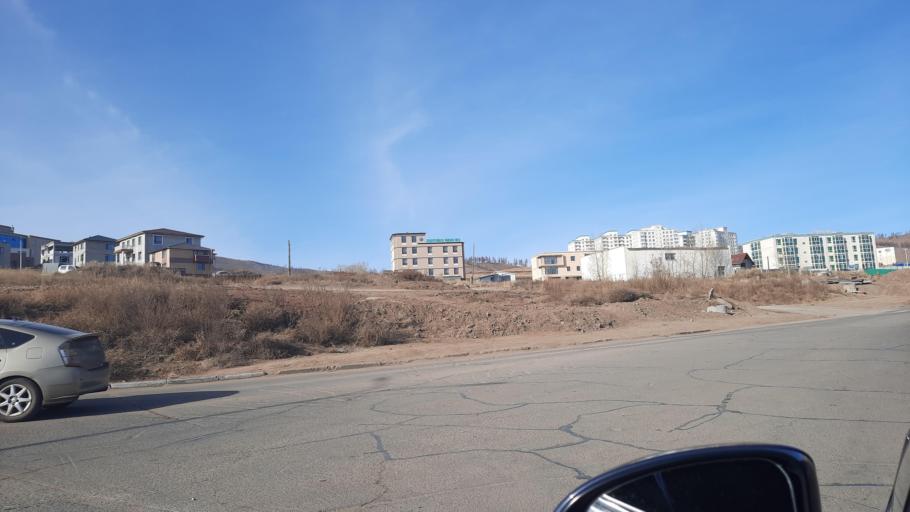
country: MN
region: Orhon
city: Erdenet
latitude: 49.0355
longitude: 104.0515
